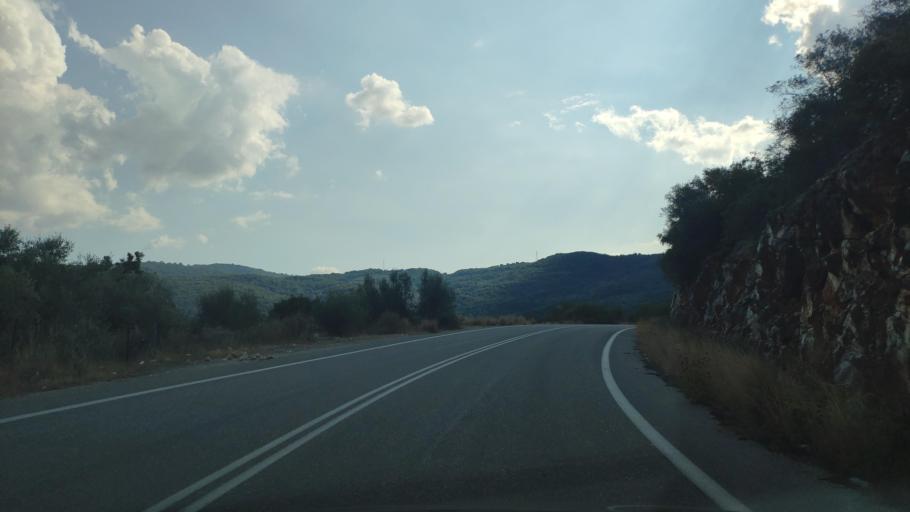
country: GR
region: West Greece
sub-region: Nomos Aitolias kai Akarnanias
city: Stanos
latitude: 38.7691
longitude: 21.1630
